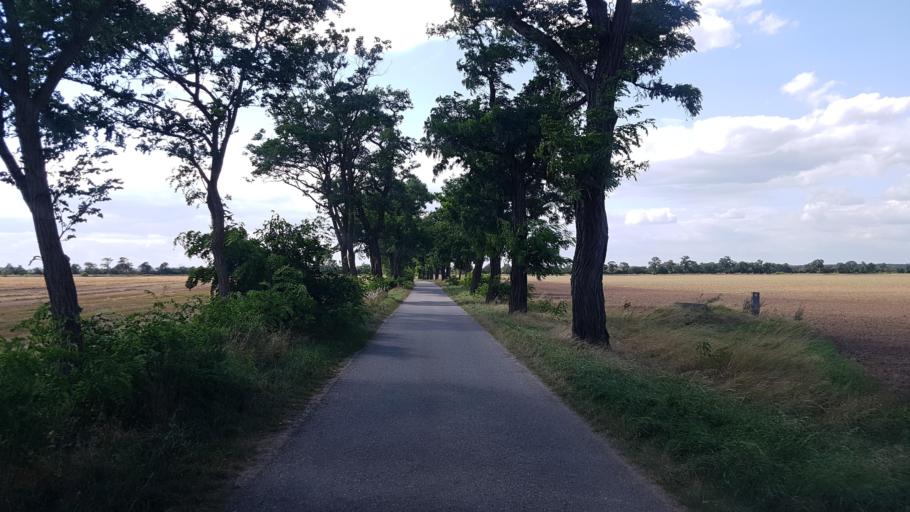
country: DE
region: Brandenburg
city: Muhlberg
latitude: 51.4356
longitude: 13.2758
